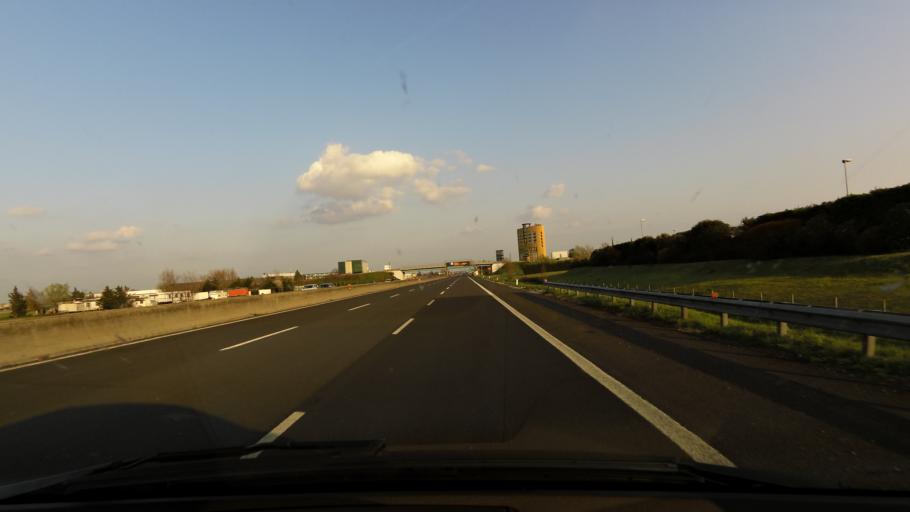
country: IT
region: Emilia-Romagna
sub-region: Provincia di Bologna
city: Imola
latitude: 44.3858
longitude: 11.7275
